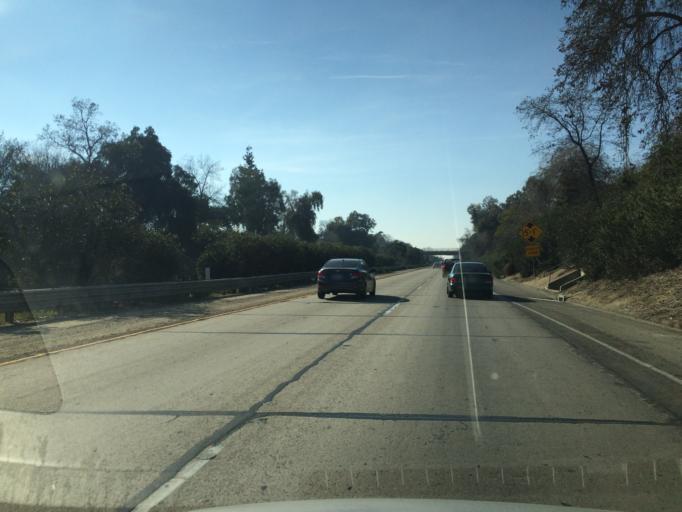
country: US
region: California
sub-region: Tulare County
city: Visalia
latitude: 36.3270
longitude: -119.3020
